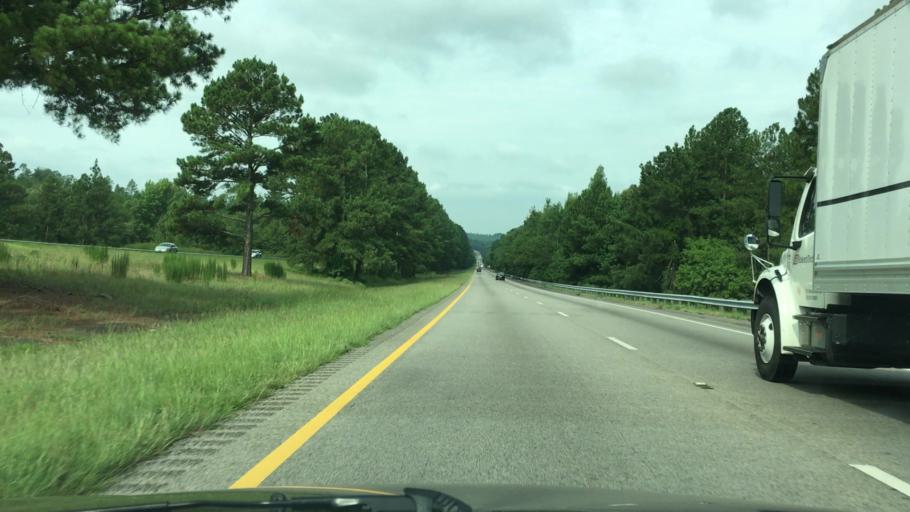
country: US
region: South Carolina
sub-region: Aiken County
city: Graniteville
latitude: 33.6323
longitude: -81.7931
